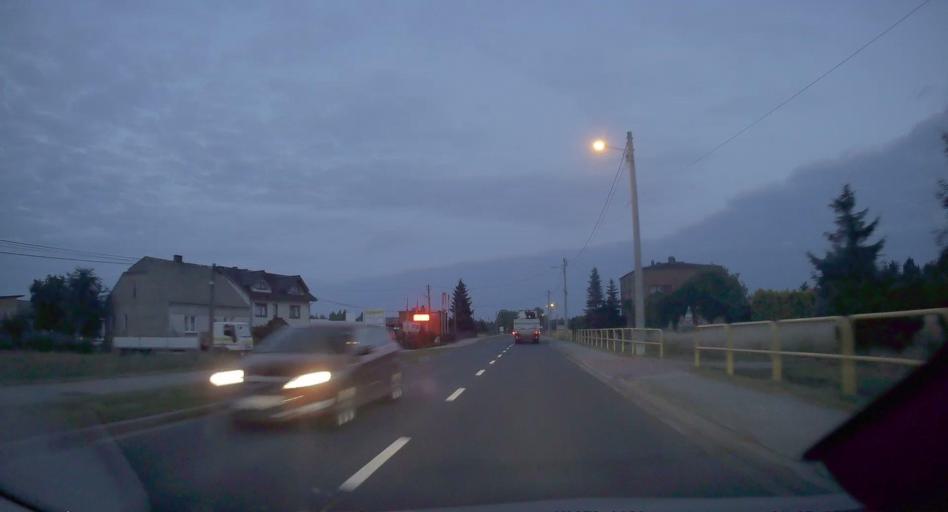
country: PL
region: Silesian Voivodeship
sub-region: Powiat klobucki
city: Opatow
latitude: 50.9246
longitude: 18.8726
